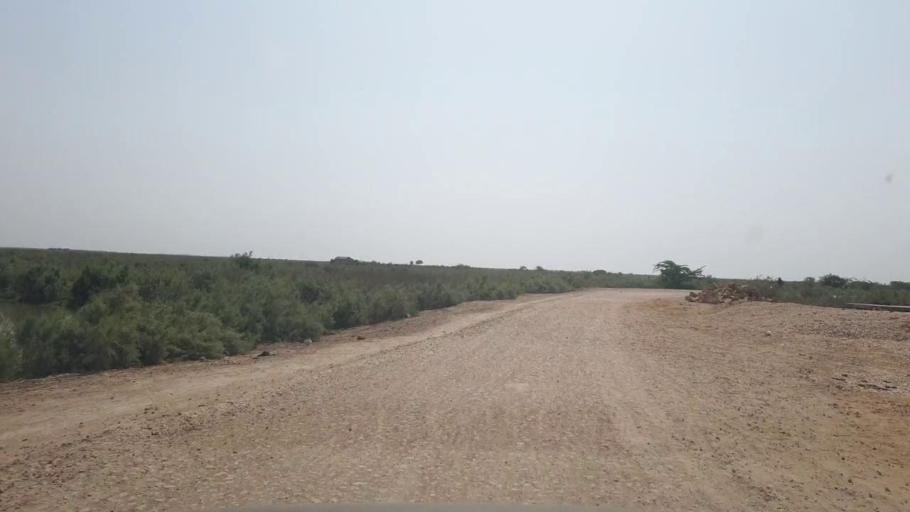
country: PK
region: Sindh
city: Jati
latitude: 24.3597
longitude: 68.5554
